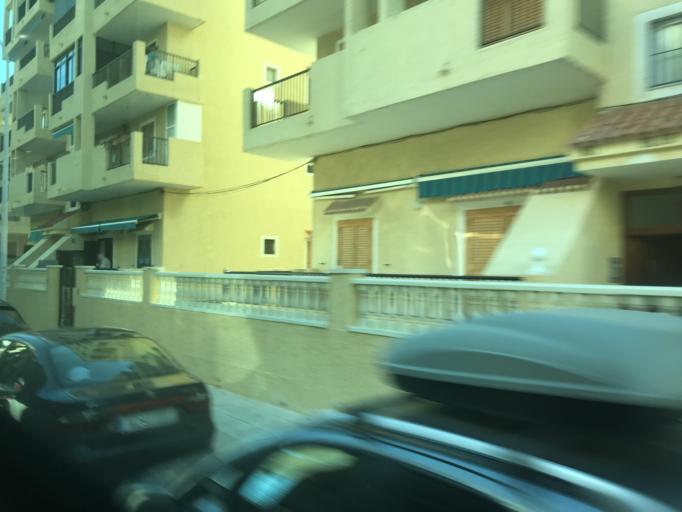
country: ES
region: Valencia
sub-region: Provincia de Alicante
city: Torrevieja
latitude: 38.0191
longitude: -0.6573
